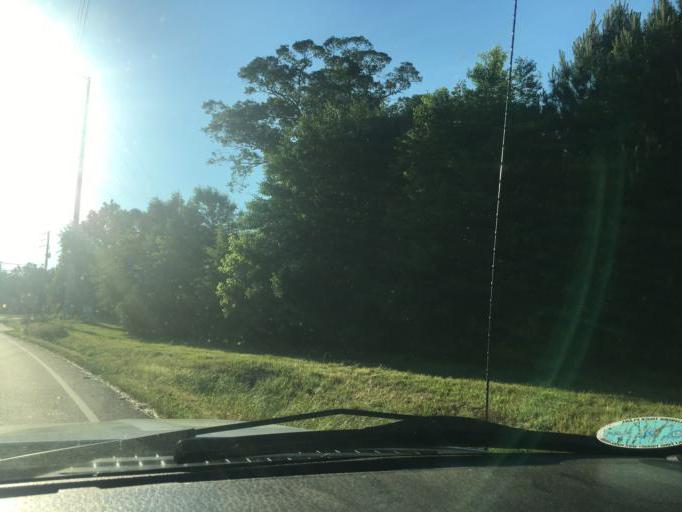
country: US
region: Georgia
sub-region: Forsyth County
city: Cumming
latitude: 34.2725
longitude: -84.1034
